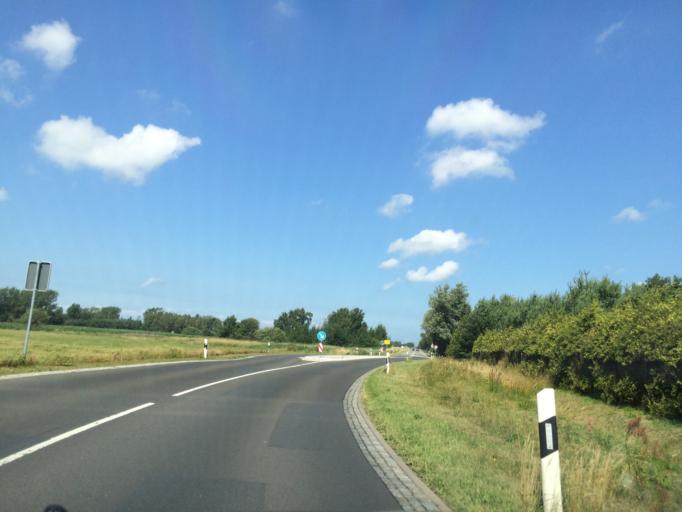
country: DE
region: Mecklenburg-Vorpommern
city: Barth
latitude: 54.3828
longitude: 12.6777
